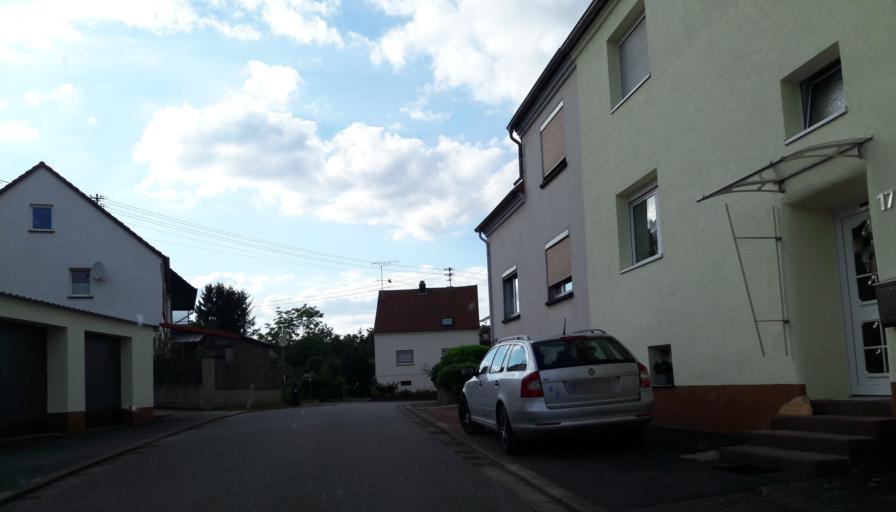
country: DE
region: Saarland
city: Mainzweiler
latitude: 49.4370
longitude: 7.1238
